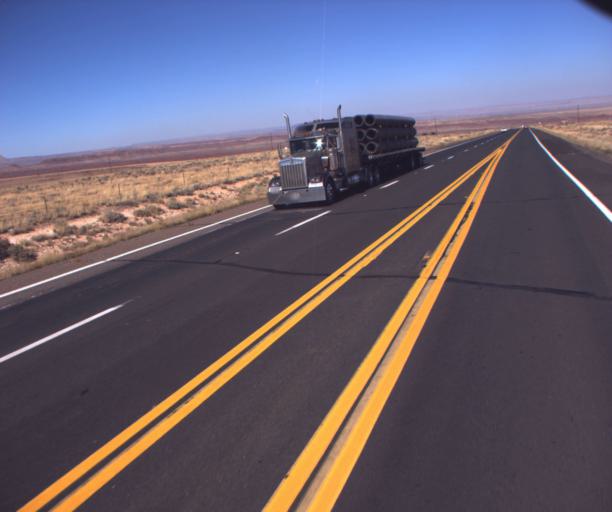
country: US
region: Arizona
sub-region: Coconino County
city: Tuba City
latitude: 35.7538
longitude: -111.4698
